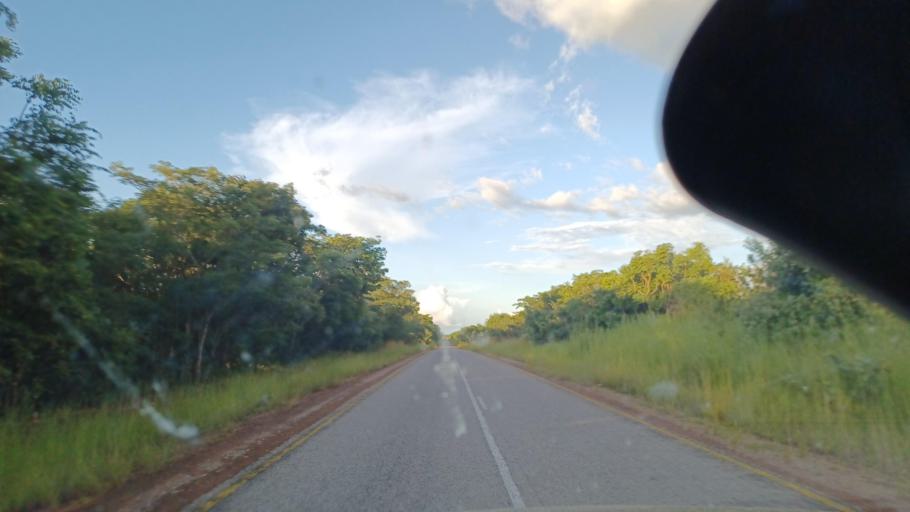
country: ZM
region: North-Western
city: Kalengwa
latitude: -13.0976
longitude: 25.2383
